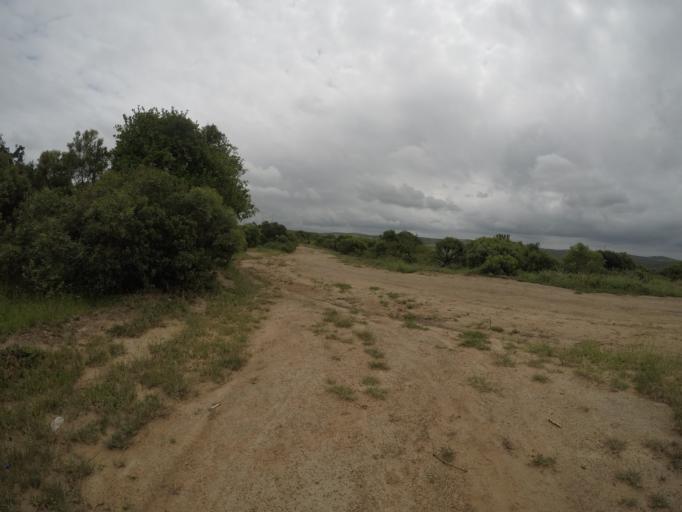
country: ZA
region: KwaZulu-Natal
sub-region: uThungulu District Municipality
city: Empangeni
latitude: -28.6058
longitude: 31.8320
